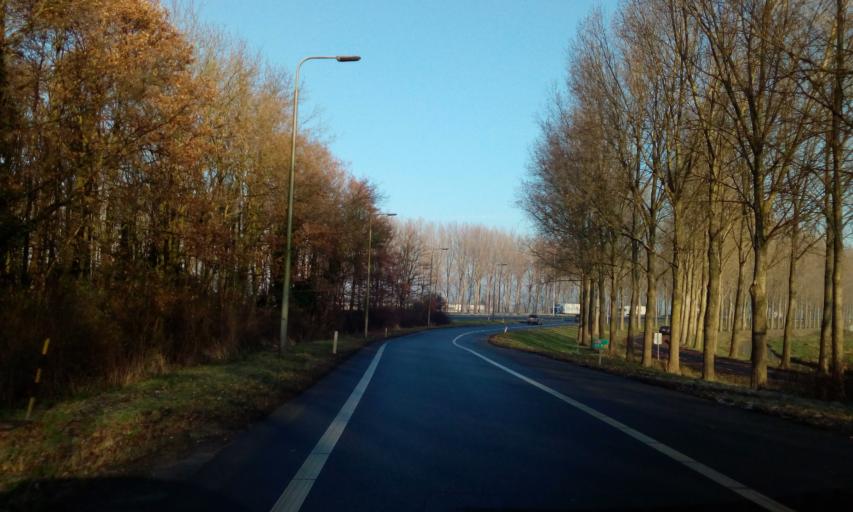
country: NL
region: South Holland
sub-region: Gemeente Krimpen aan den IJssel
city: Krimpen aan den IJssel
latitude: 51.9804
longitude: 4.6218
